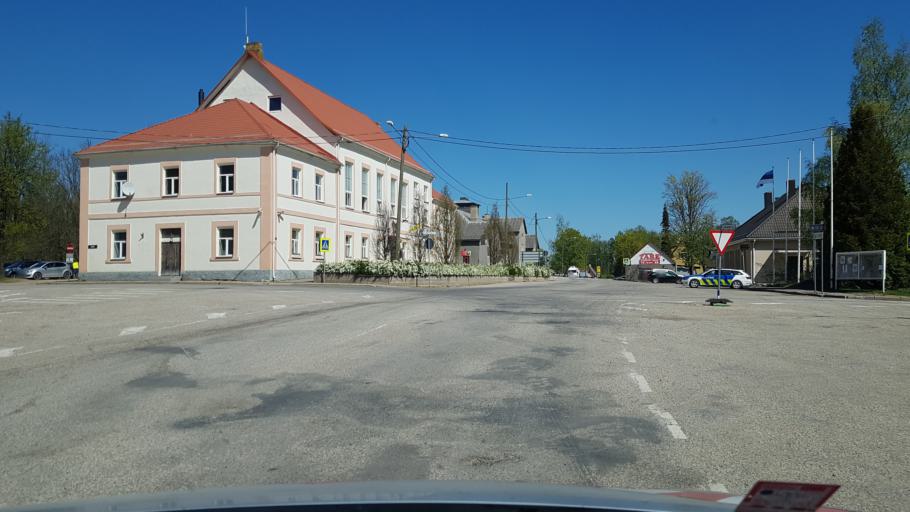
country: EE
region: Vorumaa
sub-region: Antsla vald
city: Vana-Antsla
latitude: 57.8289
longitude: 26.5279
